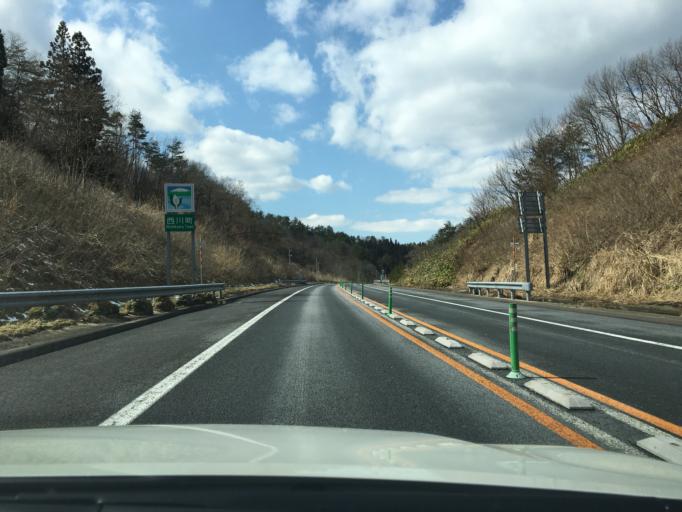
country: JP
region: Yamagata
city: Sagae
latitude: 38.4030
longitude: 140.1985
